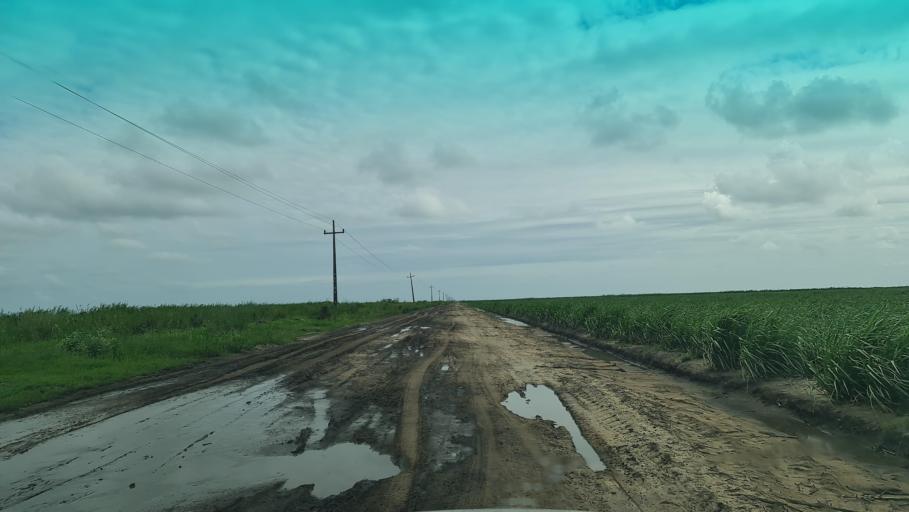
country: MZ
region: Maputo
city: Manhica
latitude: -25.4461
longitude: 32.8396
